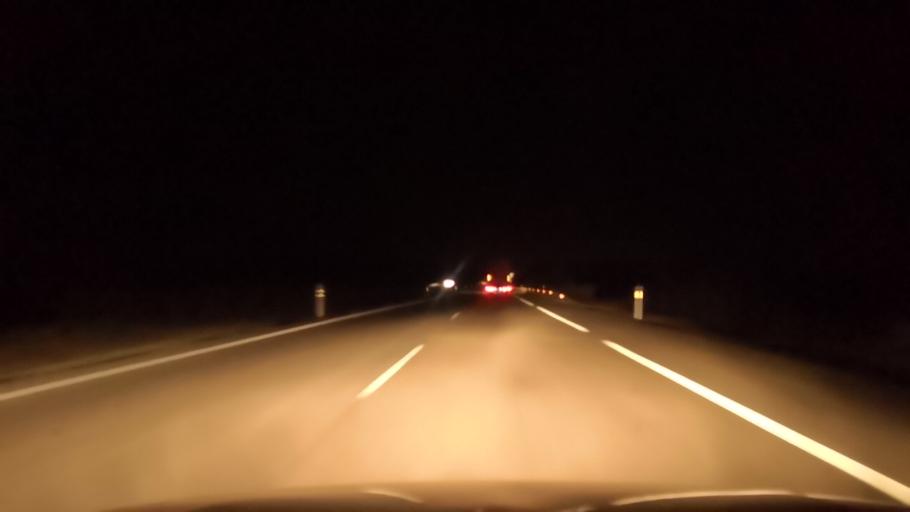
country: ES
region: Castille and Leon
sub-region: Provincia de Zamora
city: Pobladura del Valle
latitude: 42.1033
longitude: -5.7212
